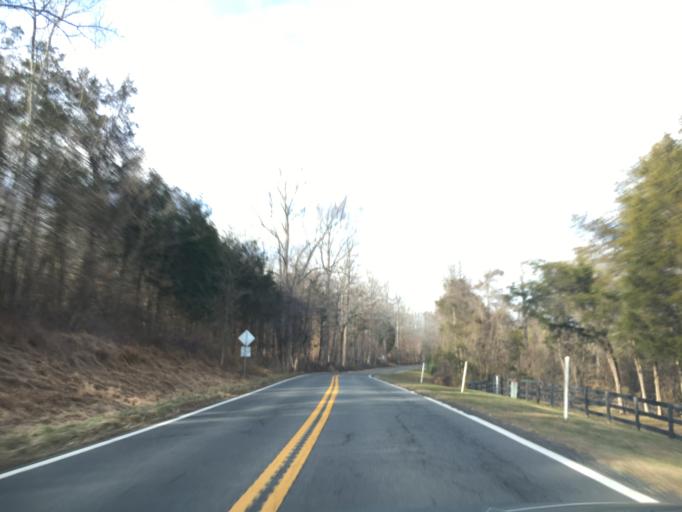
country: US
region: Virginia
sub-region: Fauquier County
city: Warrenton
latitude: 38.7033
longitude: -77.9124
